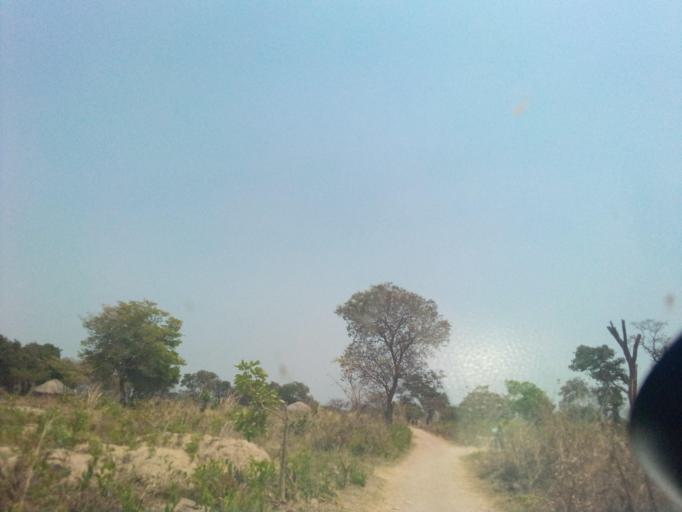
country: ZM
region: Copperbelt
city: Kataba
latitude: -12.2418
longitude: 30.3190
